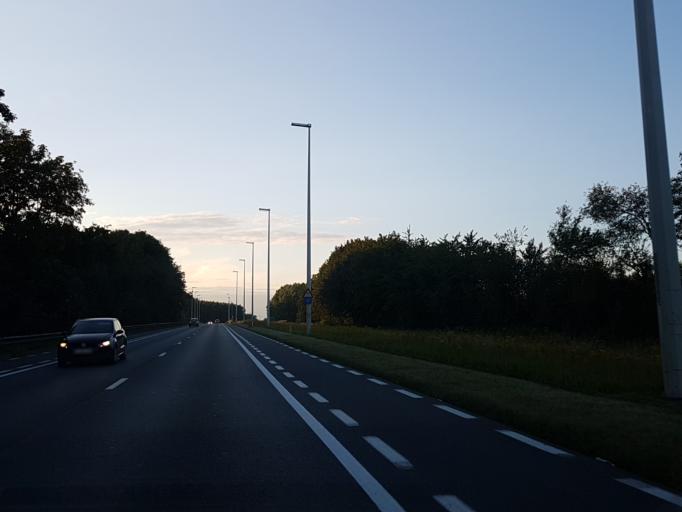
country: BE
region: Flanders
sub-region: Provincie Oost-Vlaanderen
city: Hamme
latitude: 51.1035
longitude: 4.1456
